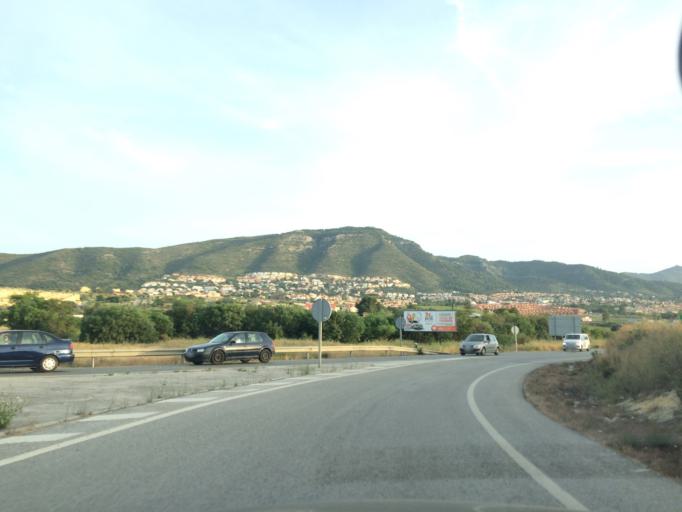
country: ES
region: Andalusia
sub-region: Provincia de Malaga
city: Alhaurin de la Torre
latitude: 36.6754
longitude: -4.5340
